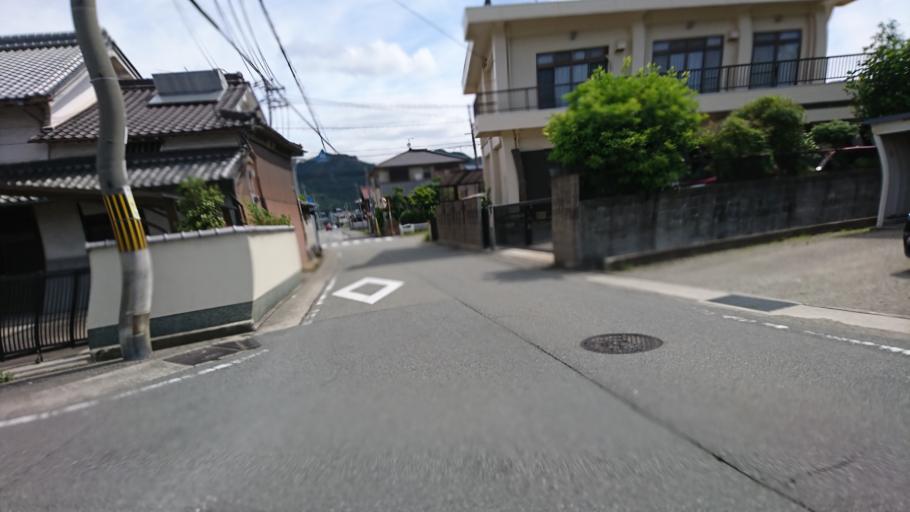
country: JP
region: Hyogo
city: Shirahamacho-usazakiminami
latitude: 34.8126
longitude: 134.7445
